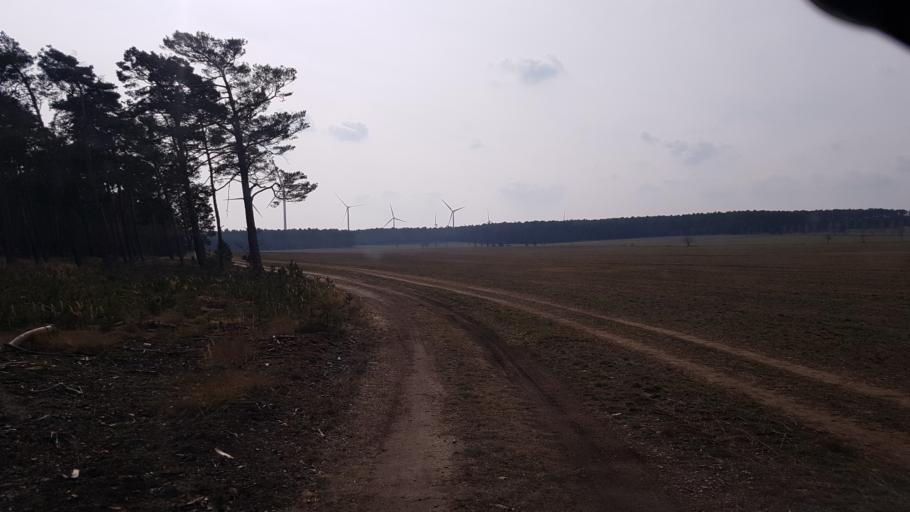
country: DE
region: Brandenburg
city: Schlieben
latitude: 51.6797
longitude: 13.3596
